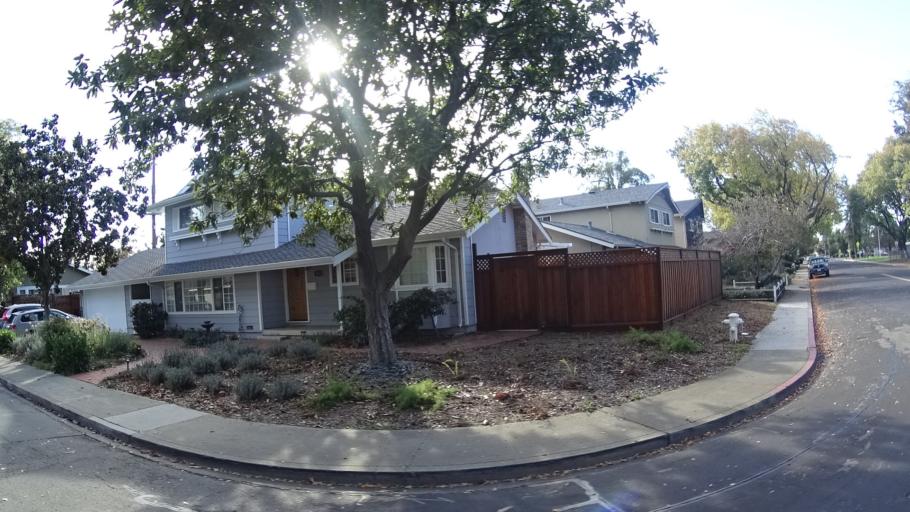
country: US
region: California
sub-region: Santa Clara County
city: Santa Clara
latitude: 37.3571
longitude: -121.9741
